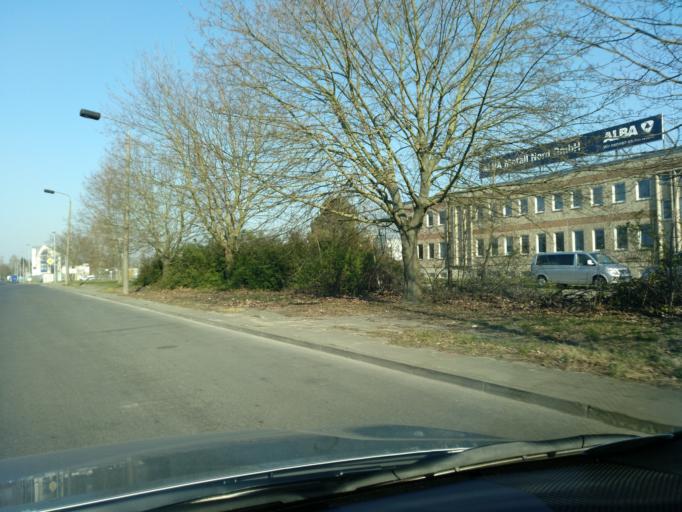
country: DE
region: Berlin
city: Mahlsdorf
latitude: 52.5084
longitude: 13.6379
